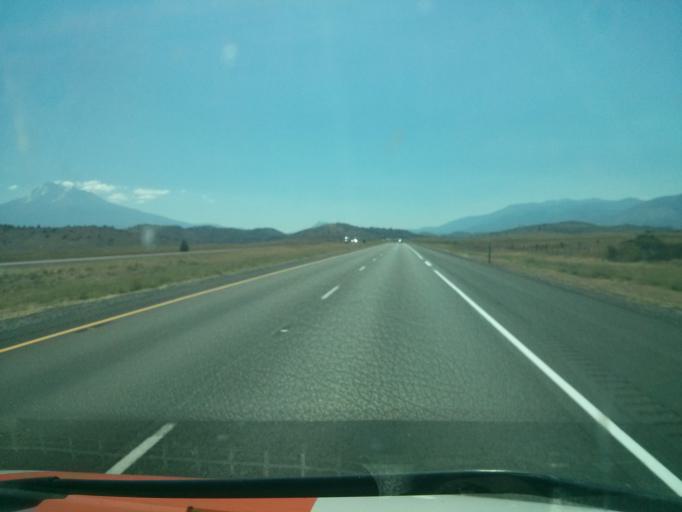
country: US
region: California
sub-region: Siskiyou County
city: Montague
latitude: 41.6182
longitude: -122.5155
